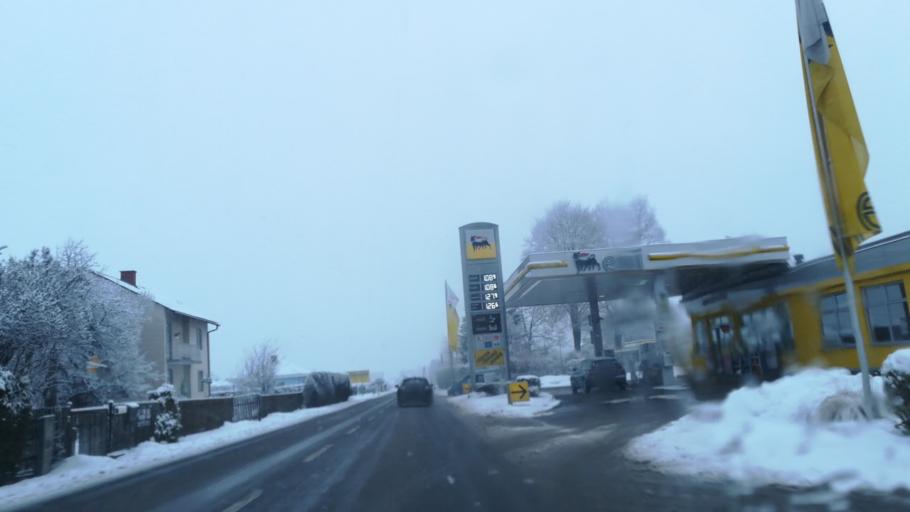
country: AT
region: Styria
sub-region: Politischer Bezirk Murtal
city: Knittelfeld
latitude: 47.2182
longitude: 14.8155
